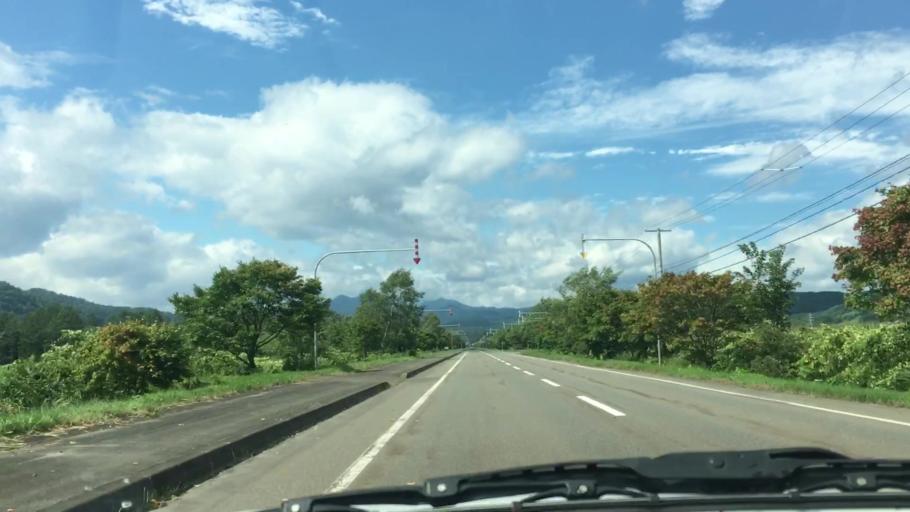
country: JP
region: Hokkaido
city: Otofuke
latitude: 43.3075
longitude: 143.3102
